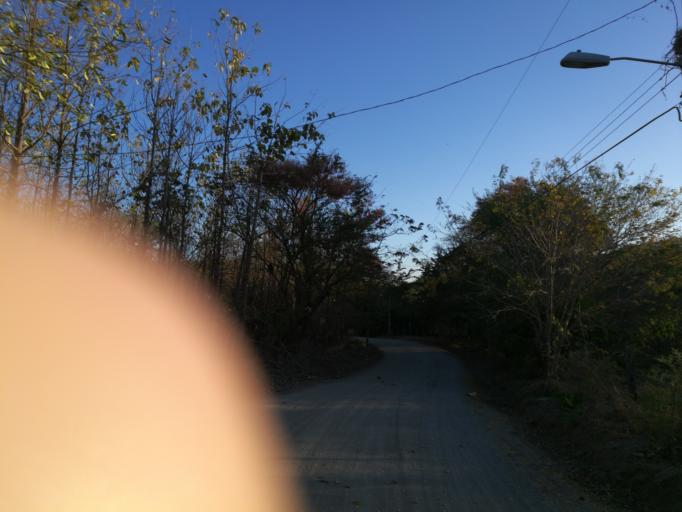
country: CR
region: Guanacaste
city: Nandayure
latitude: 10.0979
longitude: -85.1851
